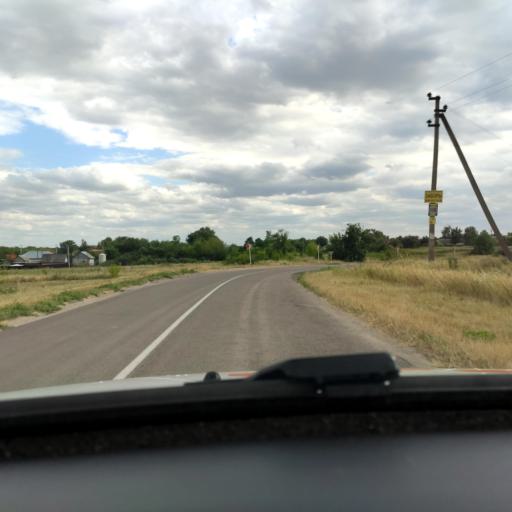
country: RU
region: Voronezj
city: Orlovo
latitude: 51.6647
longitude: 39.5748
